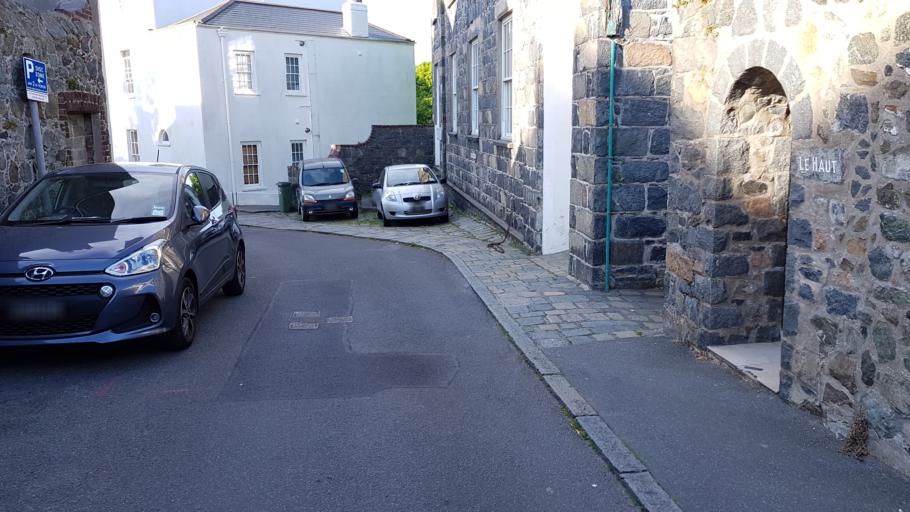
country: GG
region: St Peter Port
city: Saint Peter Port
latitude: 49.4547
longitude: -2.5386
